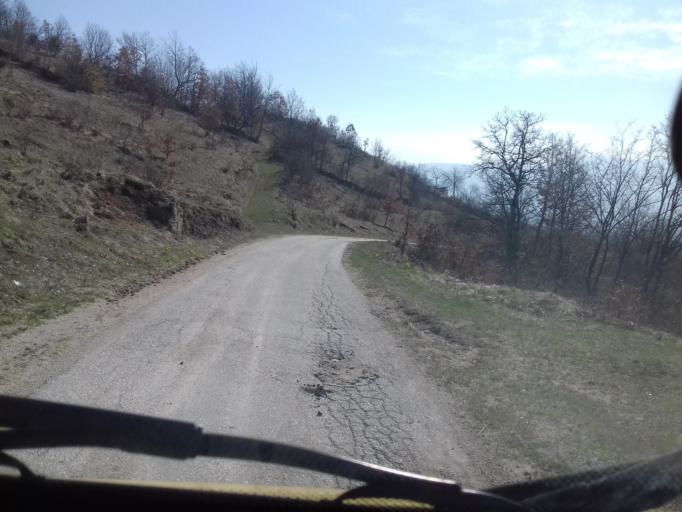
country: BA
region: Federation of Bosnia and Herzegovina
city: Travnik
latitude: 44.2490
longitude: 17.7206
